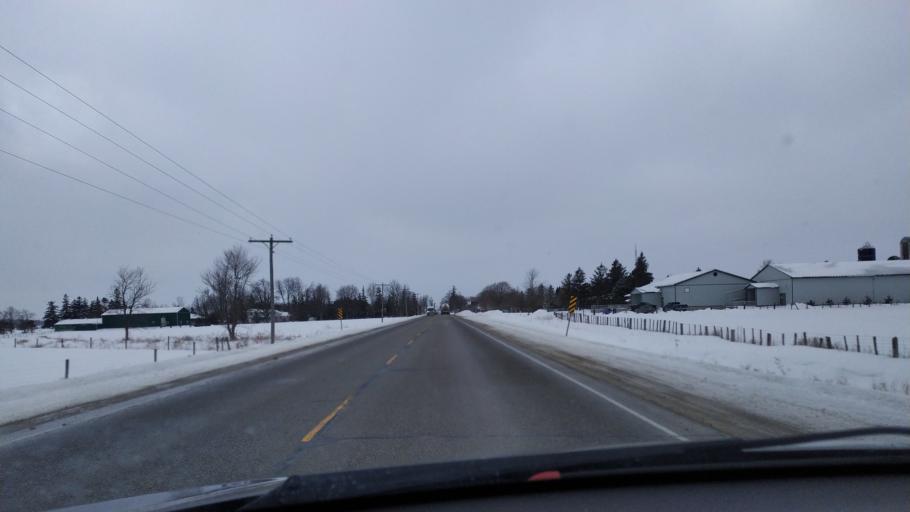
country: CA
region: Ontario
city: North Perth
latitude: 43.5864
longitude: -80.8701
